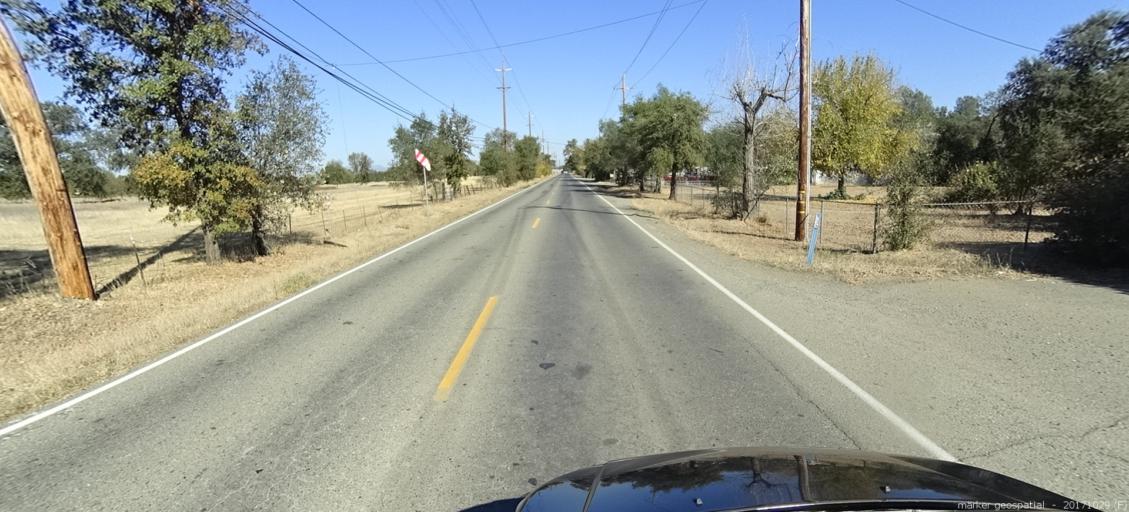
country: US
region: California
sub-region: Shasta County
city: Redding
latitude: 40.5124
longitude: -122.3866
